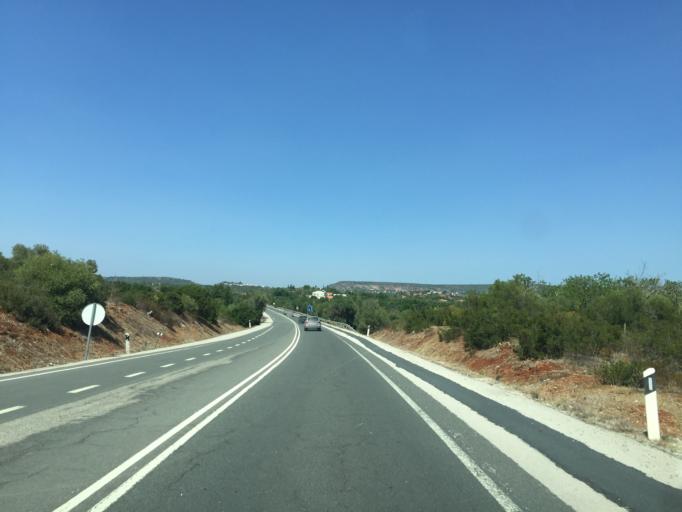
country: PT
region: Faro
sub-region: Silves
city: Sao Bartolomeu de Messines
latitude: 37.2073
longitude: -8.2576
